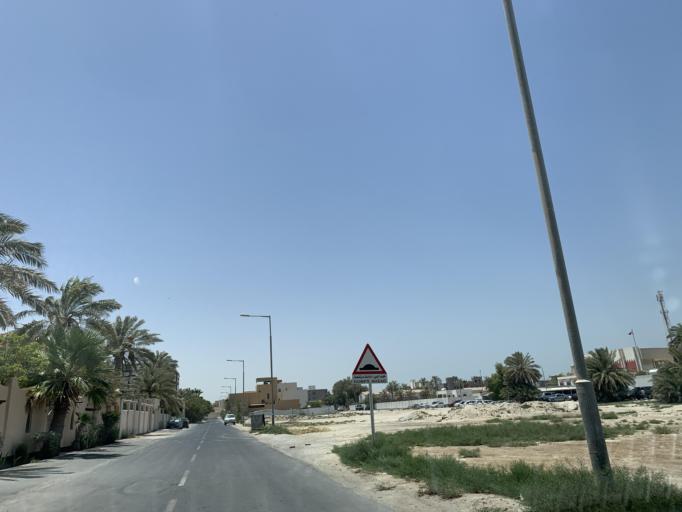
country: BH
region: Manama
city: Jidd Hafs
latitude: 26.2255
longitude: 50.4690
